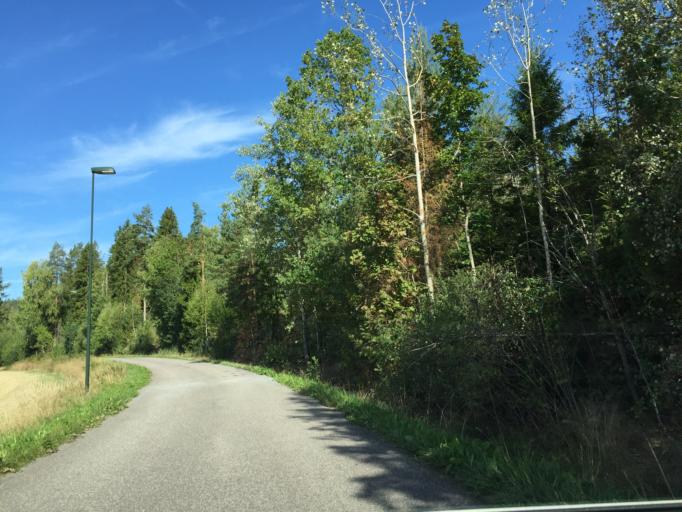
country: NO
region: Vestfold
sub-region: Holmestrand
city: Gullhaug
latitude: 59.4827
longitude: 10.1745
